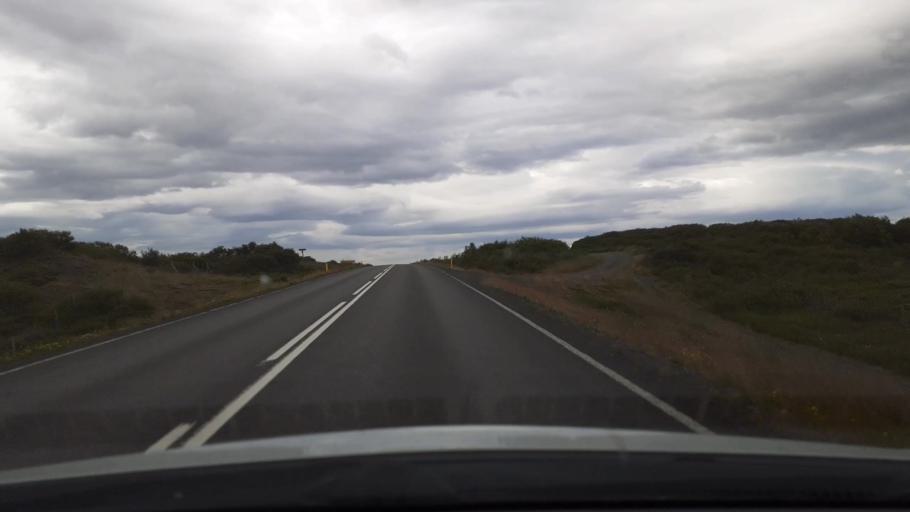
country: IS
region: West
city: Borgarnes
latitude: 64.5686
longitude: -21.9414
